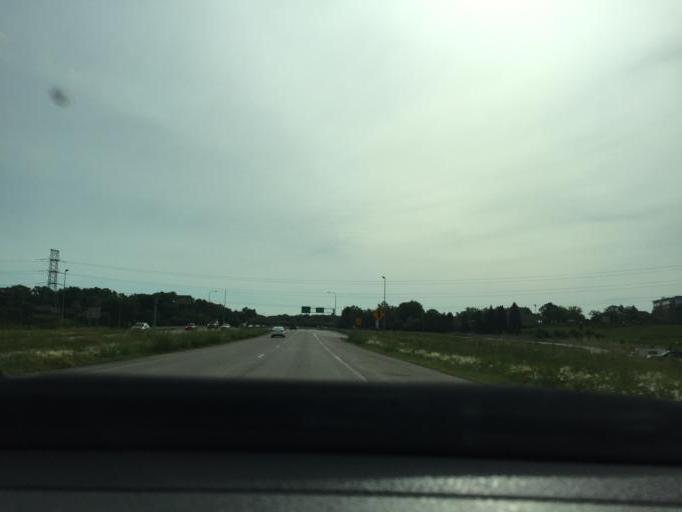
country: US
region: Minnesota
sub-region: Hennepin County
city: Hopkins
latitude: 44.9243
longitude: -93.4539
